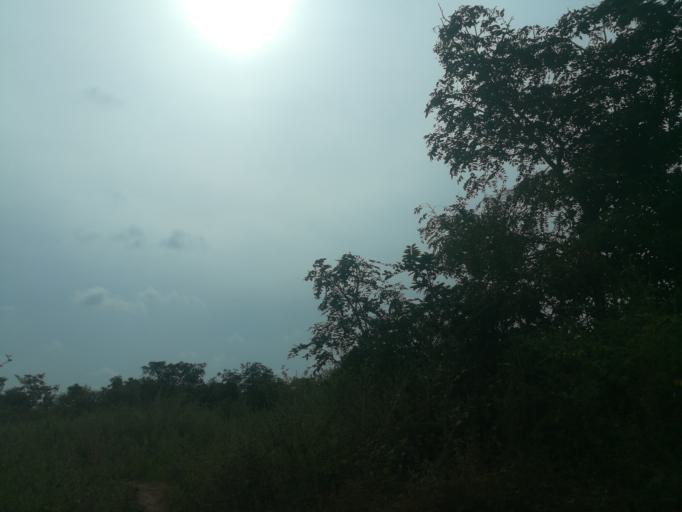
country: NG
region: Ogun
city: Ayetoro
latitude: 7.3057
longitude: 3.0740
